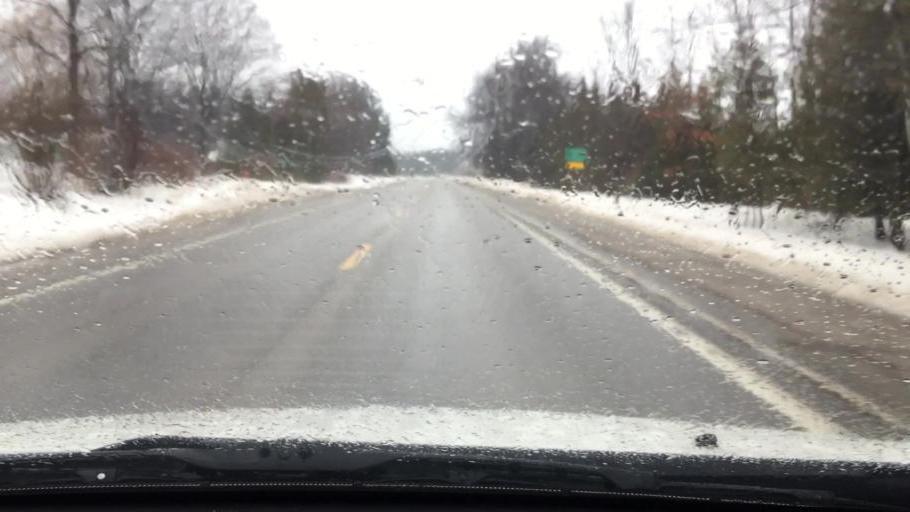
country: US
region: Michigan
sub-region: Charlevoix County
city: Charlevoix
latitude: 45.2537
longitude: -85.1857
